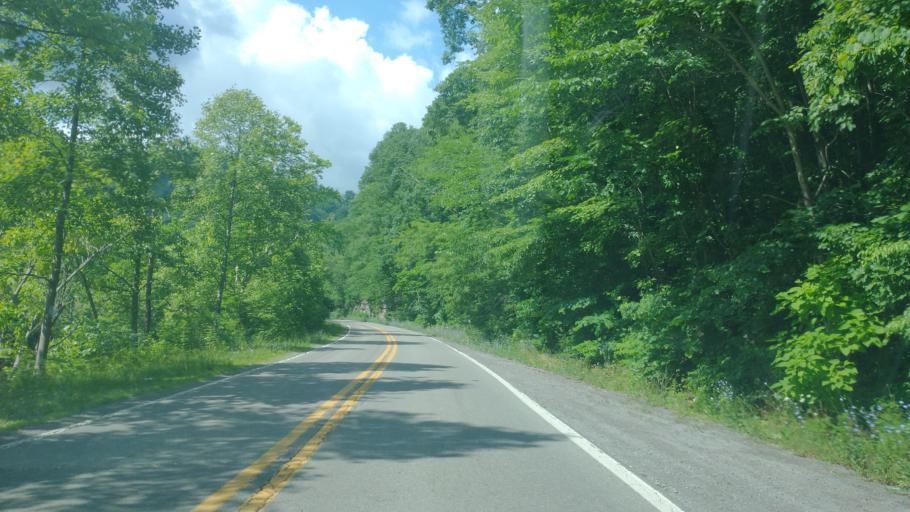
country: US
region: West Virginia
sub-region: McDowell County
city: Welch
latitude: 37.4136
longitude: -81.5281
